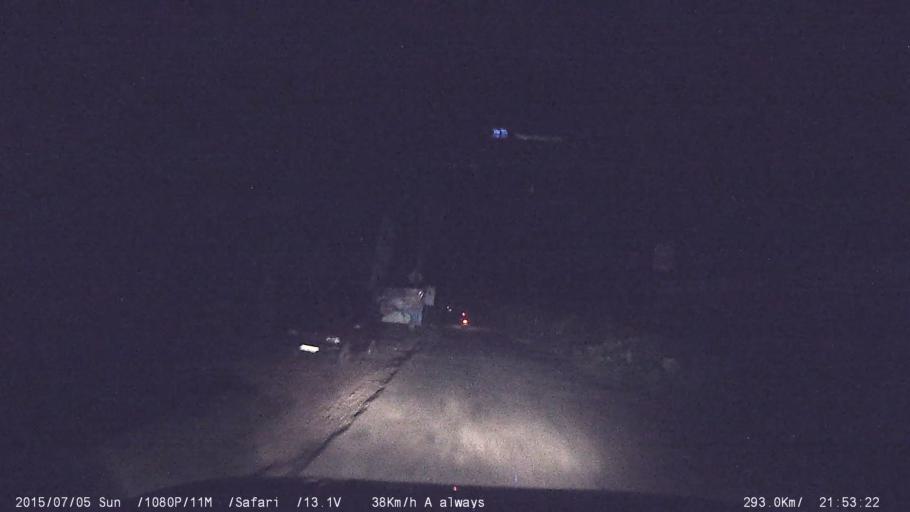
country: IN
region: Kerala
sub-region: Palakkad district
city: Mannarakkat
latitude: 10.9817
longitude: 76.4935
